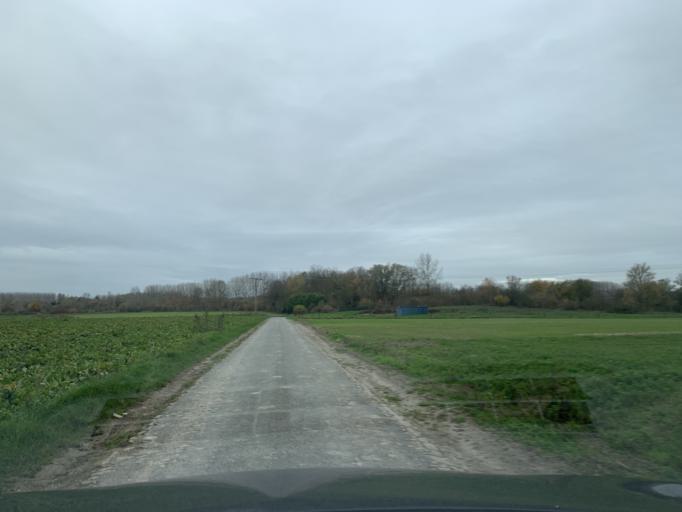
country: FR
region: Nord-Pas-de-Calais
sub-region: Departement du Pas-de-Calais
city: Oisy-le-Verger
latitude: 50.2496
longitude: 3.1029
